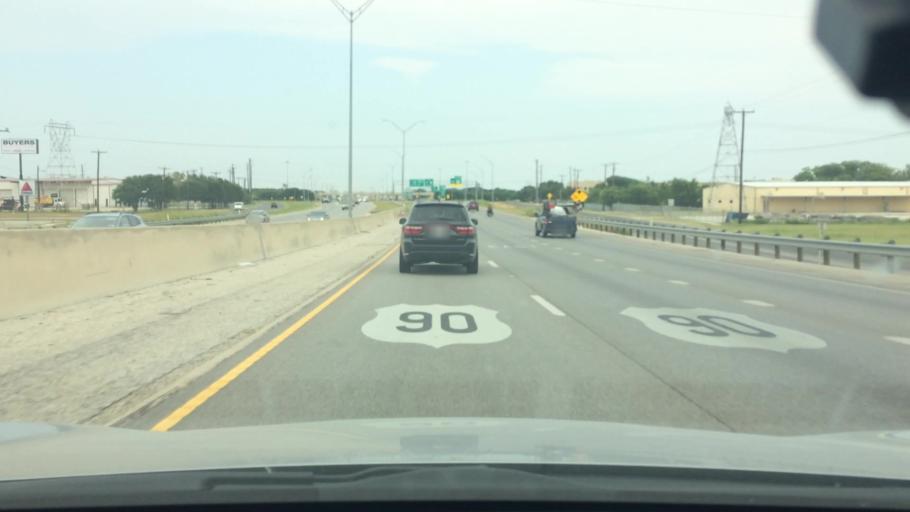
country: US
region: Texas
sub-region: Bexar County
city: Kirby
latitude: 29.4344
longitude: -98.4005
